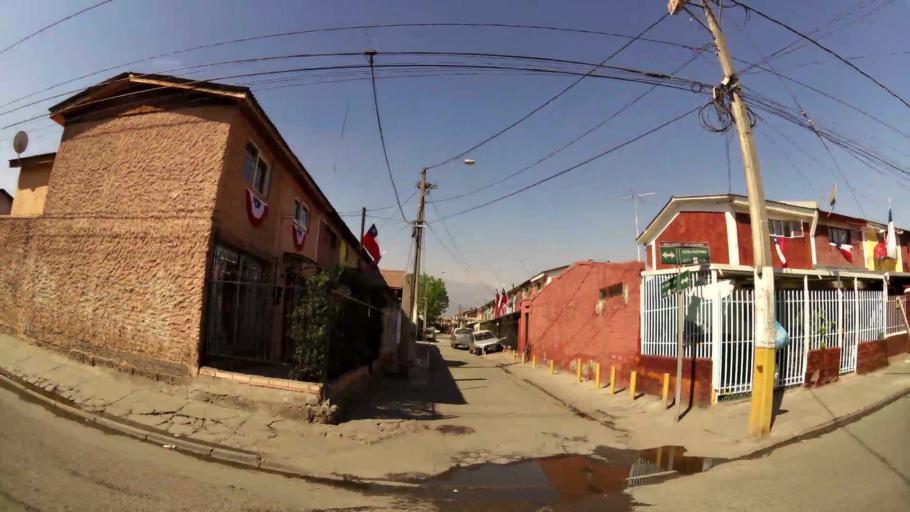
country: CL
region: Santiago Metropolitan
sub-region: Provincia de Santiago
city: La Pintana
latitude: -33.5601
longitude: -70.6271
